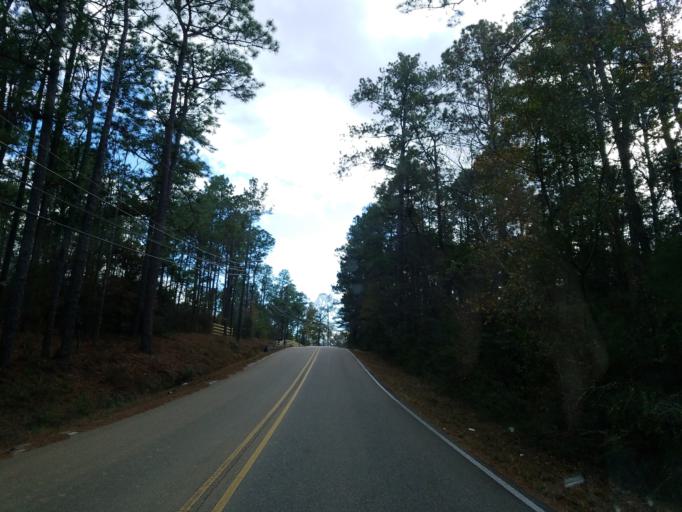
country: US
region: Mississippi
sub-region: Lamar County
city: West Hattiesburg
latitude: 31.2883
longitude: -89.3478
